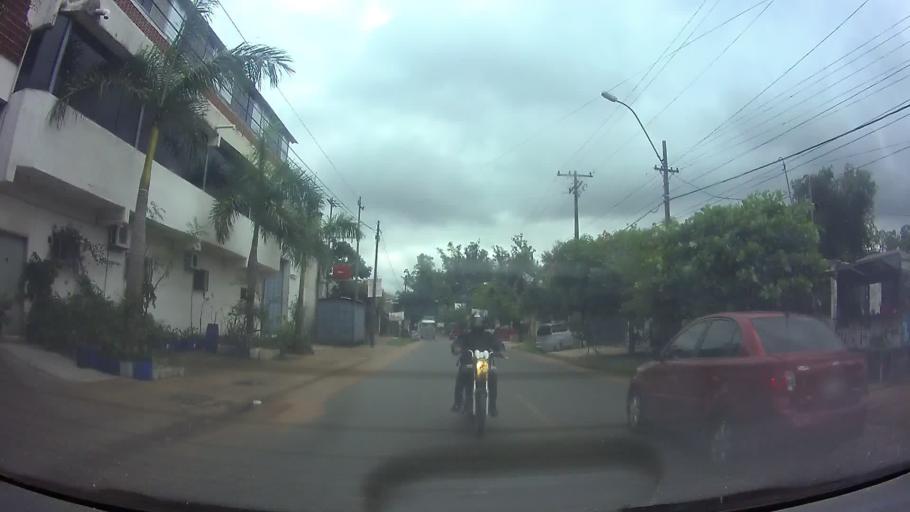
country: PY
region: Central
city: Nemby
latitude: -25.3847
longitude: -57.5481
